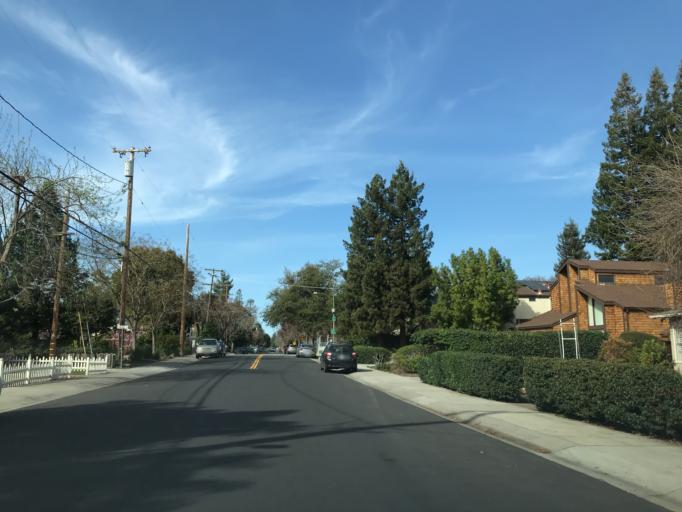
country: US
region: California
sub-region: Santa Clara County
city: Palo Alto
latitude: 37.4287
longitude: -122.1280
